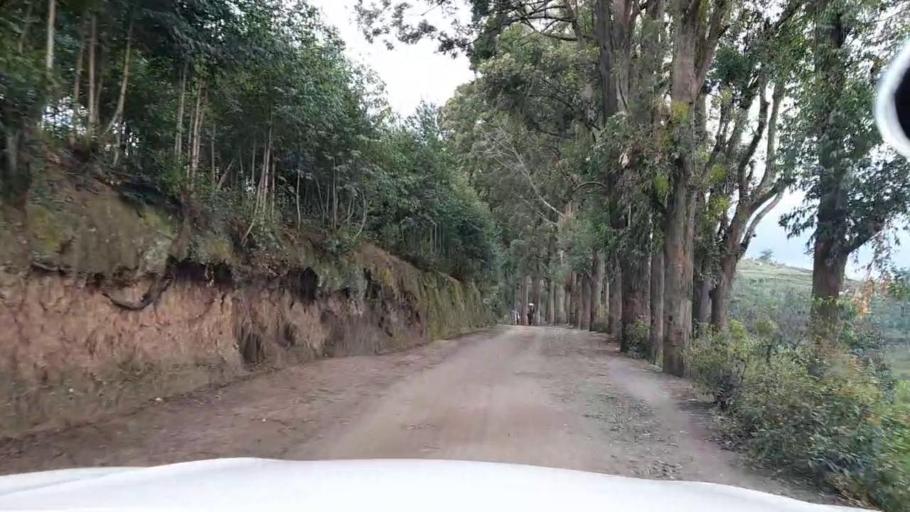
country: BI
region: Kayanza
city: Kayanza
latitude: -2.7952
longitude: 29.5095
